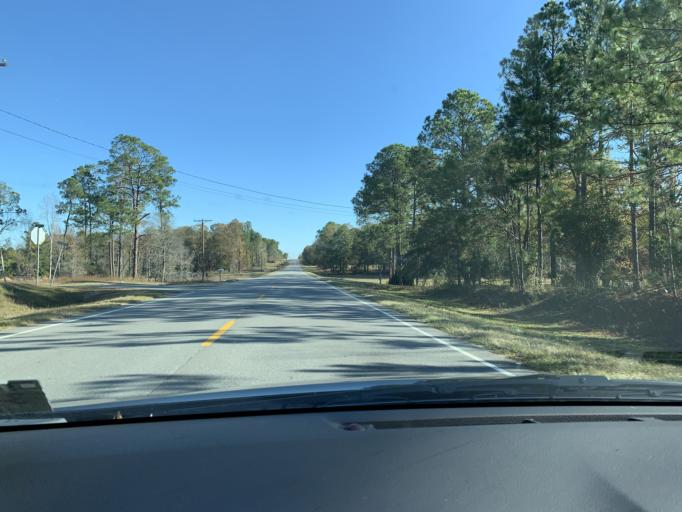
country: US
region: Georgia
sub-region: Ben Hill County
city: Fitzgerald
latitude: 31.7380
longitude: -83.1601
